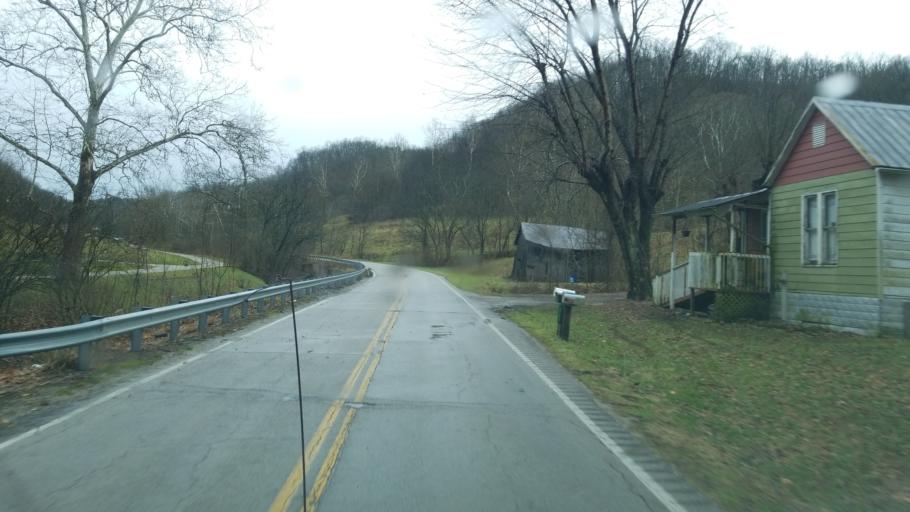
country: US
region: Kentucky
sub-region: Mason County
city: Maysville
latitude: 38.6283
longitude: -83.7072
